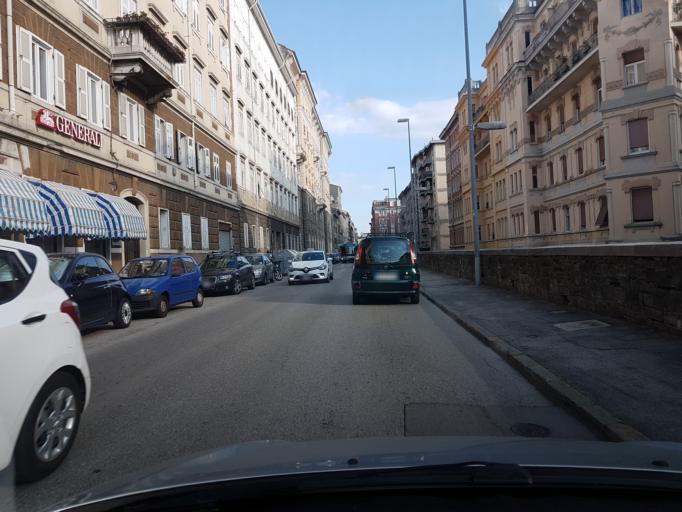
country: IT
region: Friuli Venezia Giulia
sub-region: Provincia di Trieste
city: Trieste
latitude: 45.6633
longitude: 13.7708
